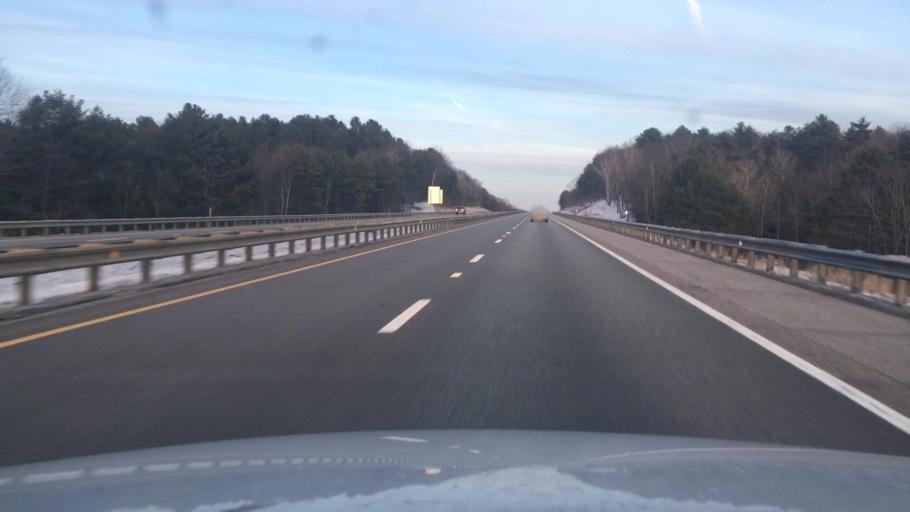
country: US
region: Maine
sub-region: Androscoggin County
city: Sabattus
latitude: 44.1173
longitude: -70.0530
